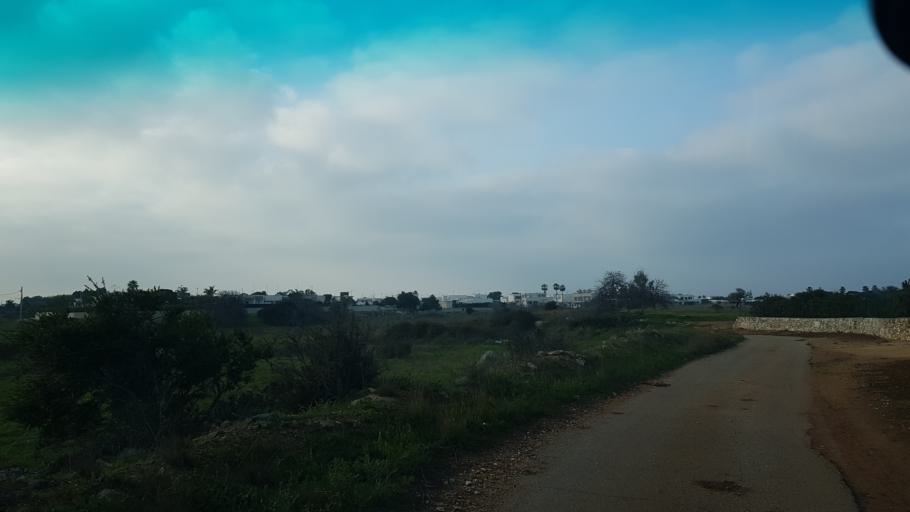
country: IT
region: Apulia
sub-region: Provincia di Brindisi
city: Carovigno
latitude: 40.7434
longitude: 17.7213
